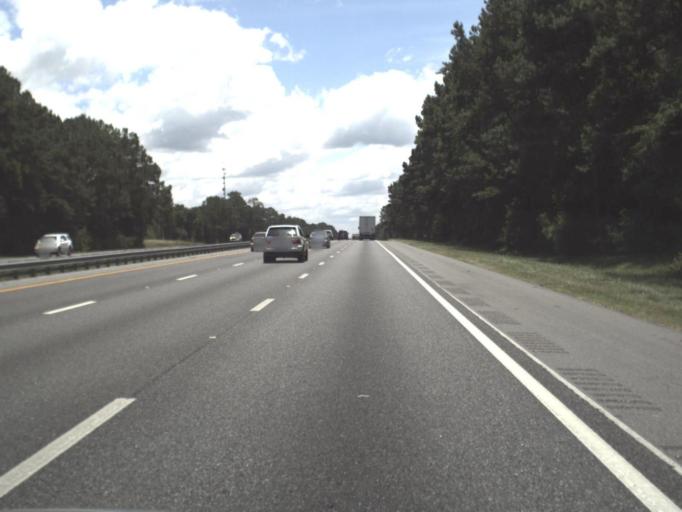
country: US
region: Florida
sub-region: Columbia County
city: Lake City
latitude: 30.0375
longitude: -82.6166
